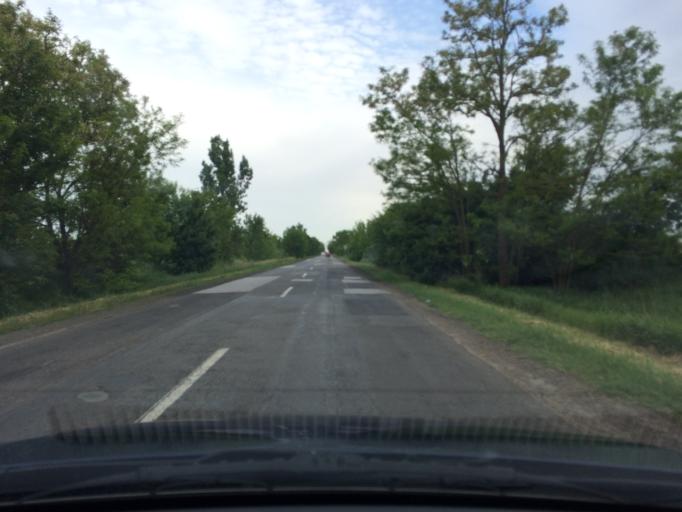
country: HU
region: Szabolcs-Szatmar-Bereg
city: Tiszavasvari
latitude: 47.9156
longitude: 21.3972
